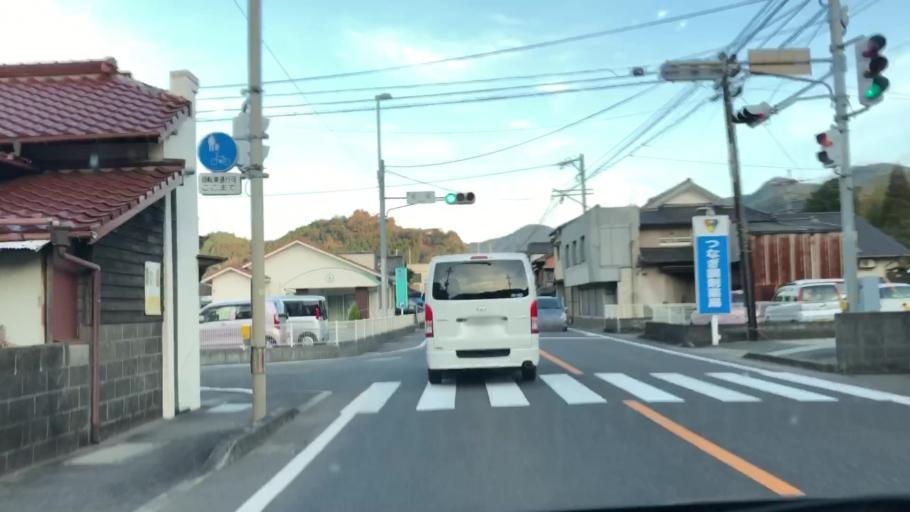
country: JP
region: Kumamoto
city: Minamata
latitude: 32.2335
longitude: 130.4480
